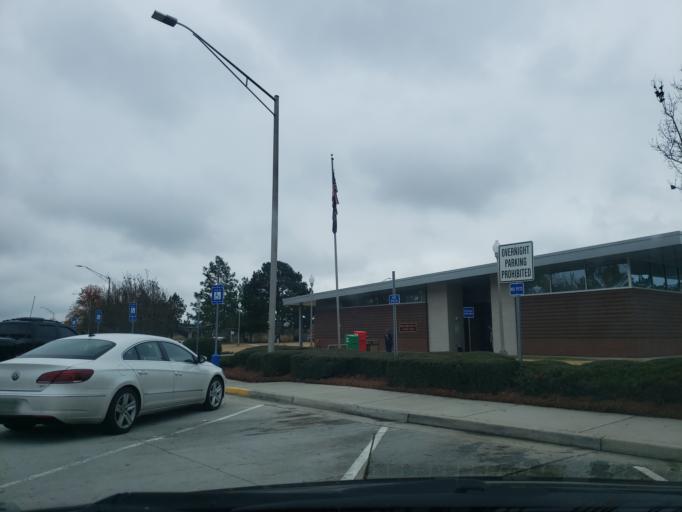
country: US
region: Georgia
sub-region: Laurens County
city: Dublin
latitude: 32.5086
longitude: -83.0483
